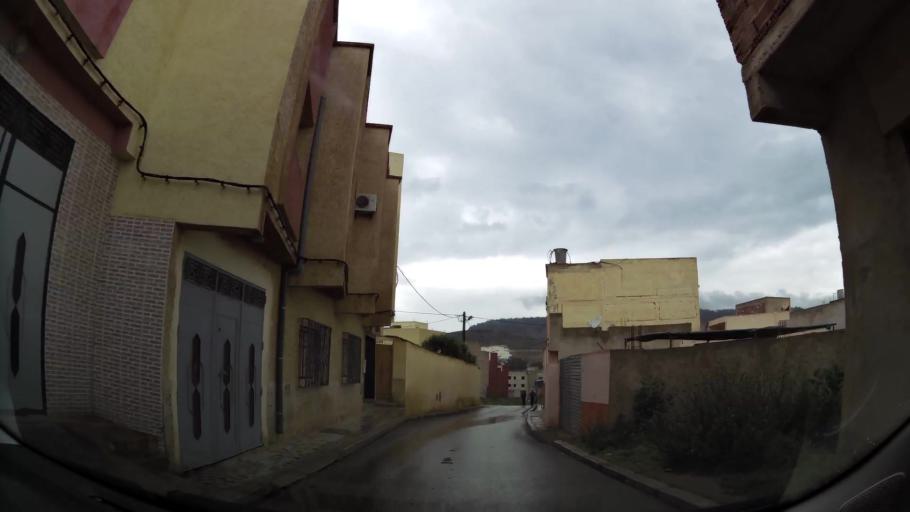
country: MA
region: Oriental
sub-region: Nador
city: Nador
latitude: 35.1466
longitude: -3.0029
